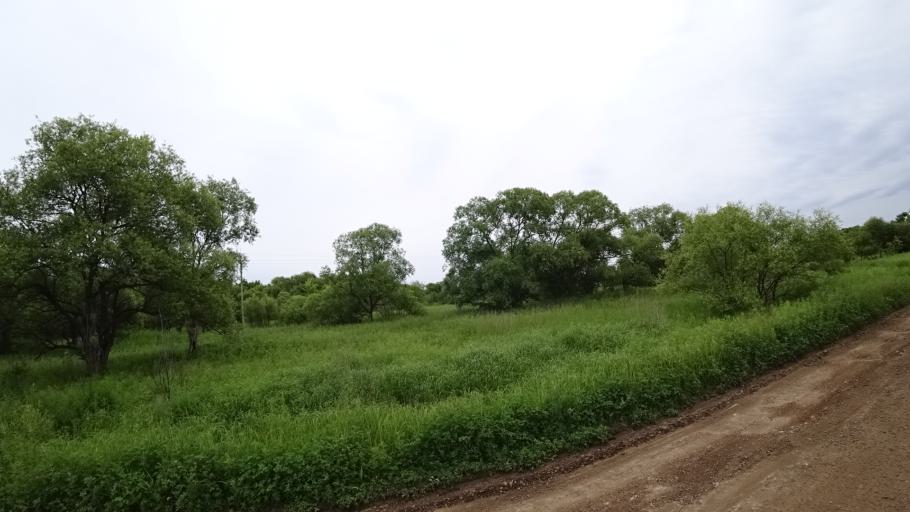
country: RU
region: Primorskiy
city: Novosysoyevka
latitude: 44.2081
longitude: 133.3286
